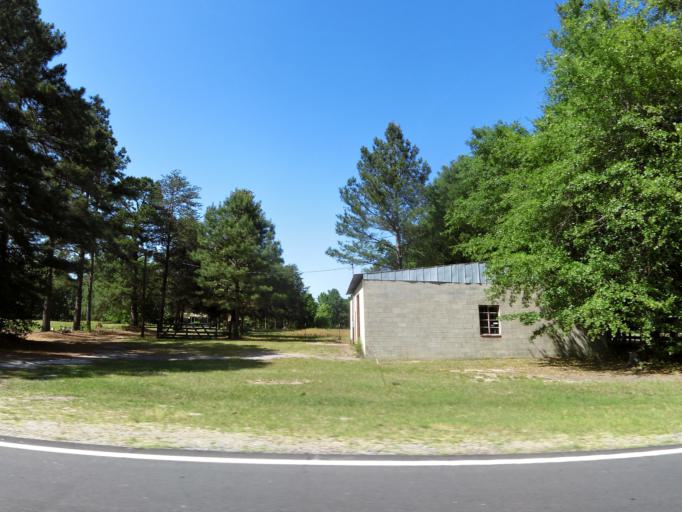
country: US
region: South Carolina
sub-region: Barnwell County
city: Williston
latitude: 33.4132
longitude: -81.4610
